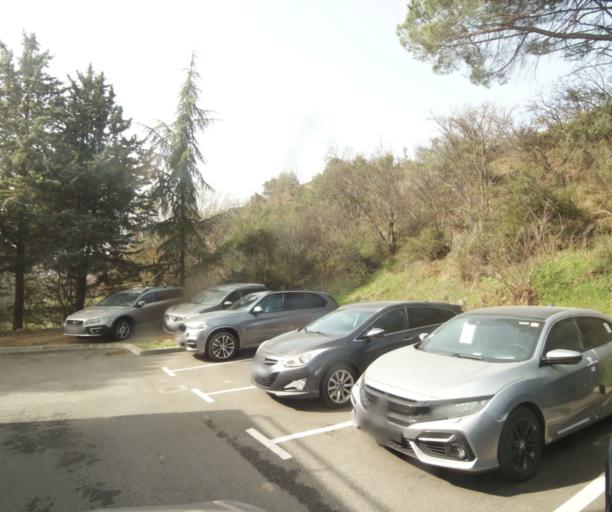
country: FR
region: Provence-Alpes-Cote d'Azur
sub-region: Departement des Bouches-du-Rhone
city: Aix-en-Provence
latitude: 43.5122
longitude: 5.4207
